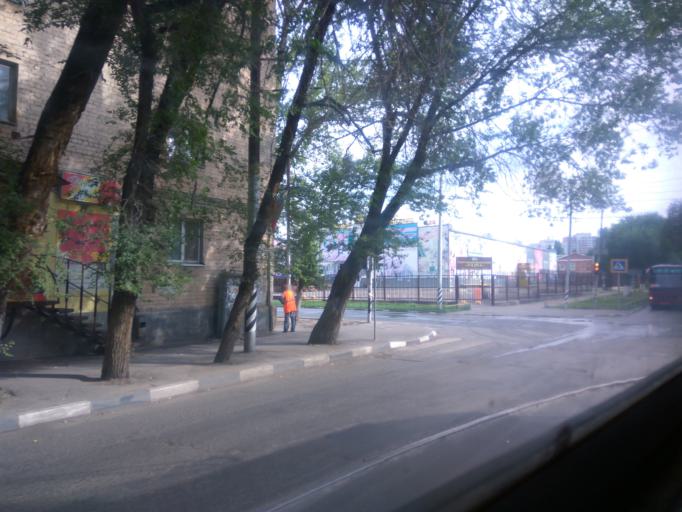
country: RU
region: Saratov
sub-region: Saratovskiy Rayon
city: Saratov
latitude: 51.5361
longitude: 45.9999
